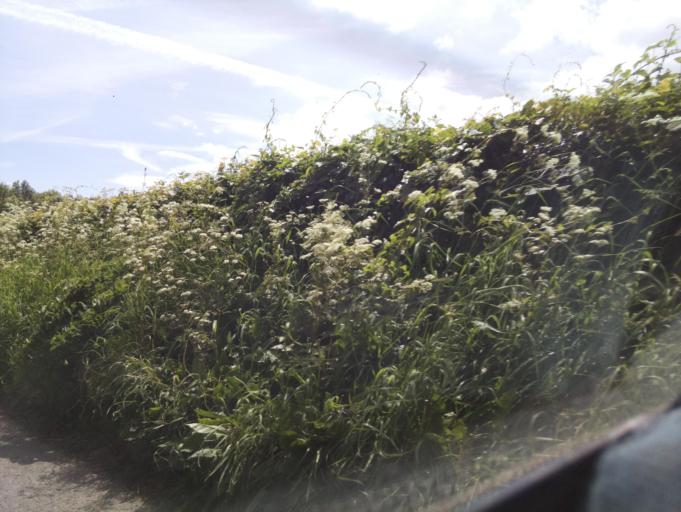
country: GB
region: England
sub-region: Herefordshire
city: Llanrothal
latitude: 51.8561
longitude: -2.8062
